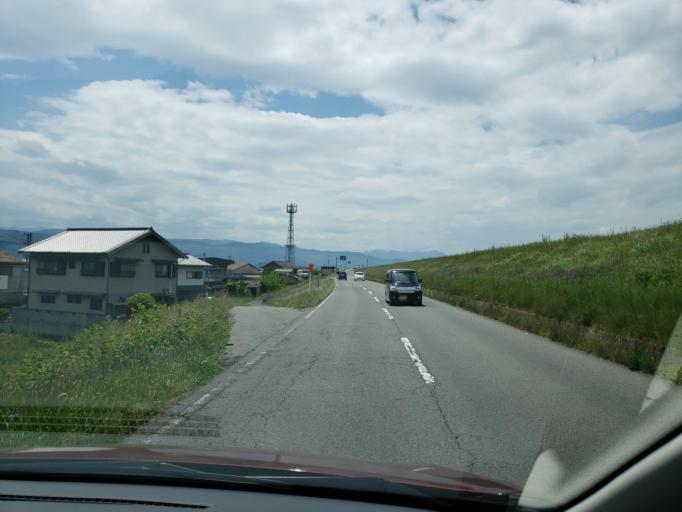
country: JP
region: Tokushima
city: Ishii
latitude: 34.0995
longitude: 134.4274
